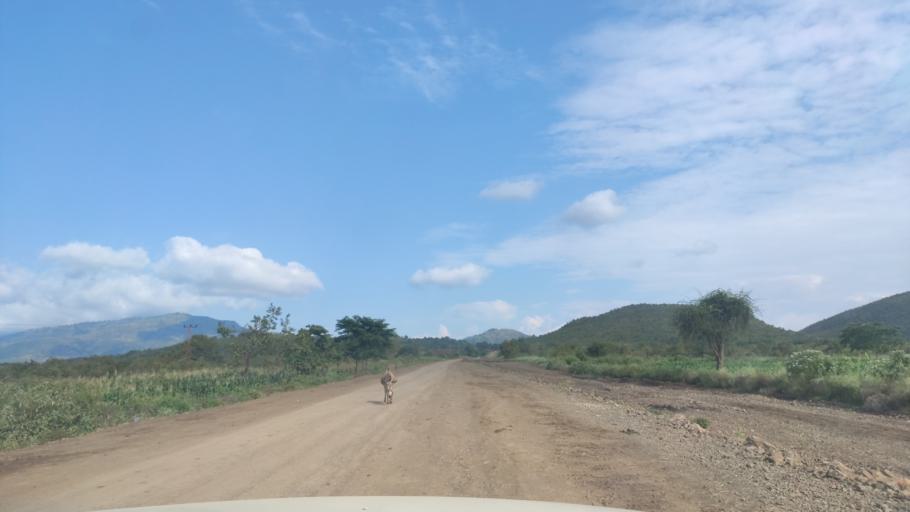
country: ET
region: Southern Nations, Nationalities, and People's Region
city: Felege Neway
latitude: 6.4341
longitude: 37.2857
